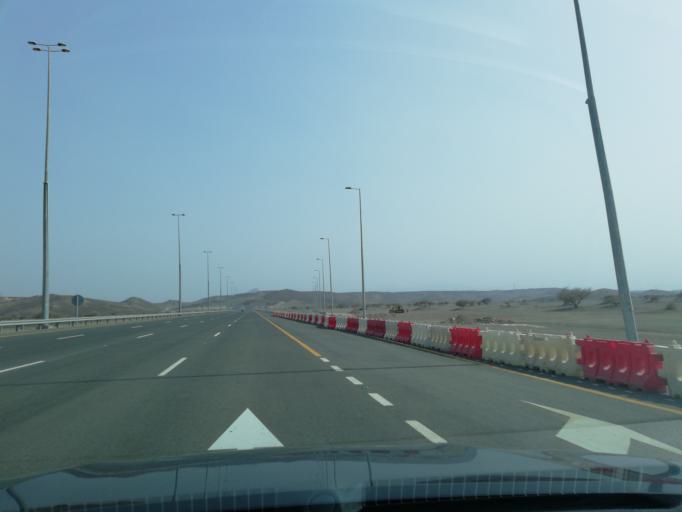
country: OM
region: Al Batinah
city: Al Liwa'
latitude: 24.3669
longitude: 56.5529
